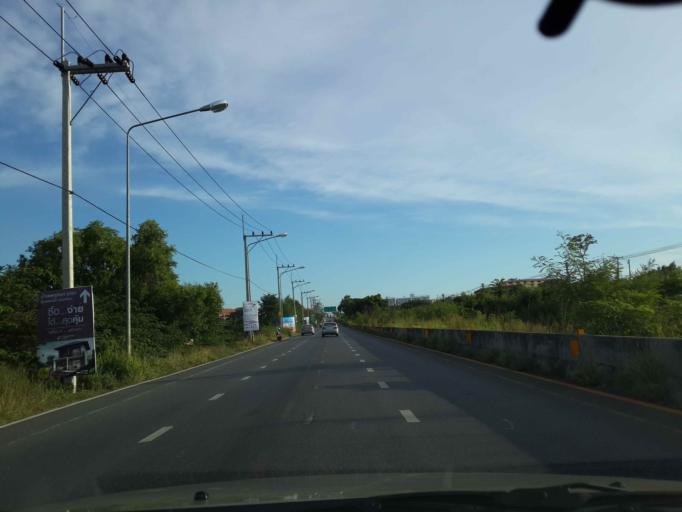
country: TH
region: Chon Buri
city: Phatthaya
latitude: 12.9395
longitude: 100.9094
